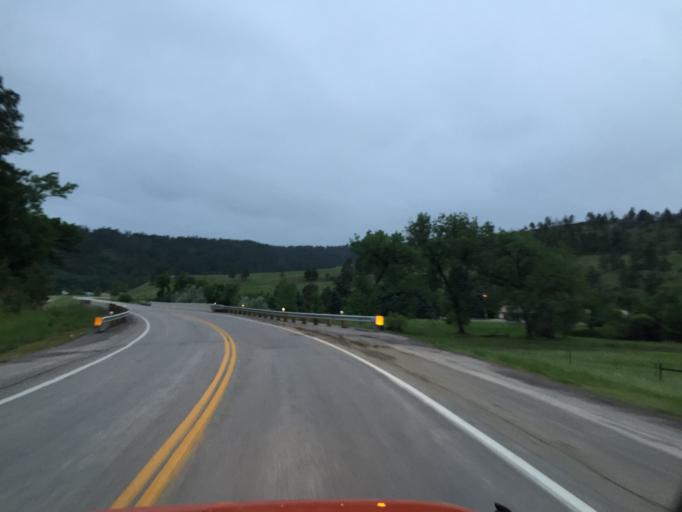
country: US
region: South Dakota
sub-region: Pennington County
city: Colonial Pine Hills
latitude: 43.8297
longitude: -103.2391
